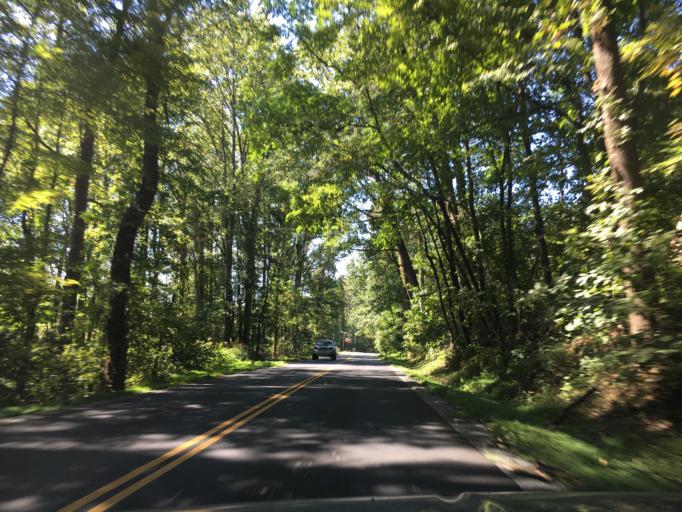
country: US
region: Virginia
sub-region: Albemarle County
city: Crozet
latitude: 37.9801
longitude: -78.7044
